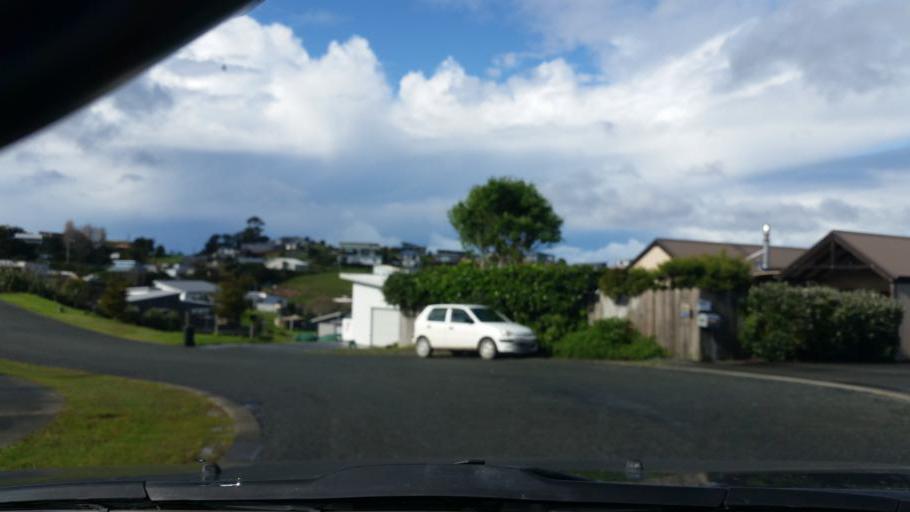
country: NZ
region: Auckland
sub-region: Auckland
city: Wellsford
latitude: -36.0874
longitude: 174.5772
